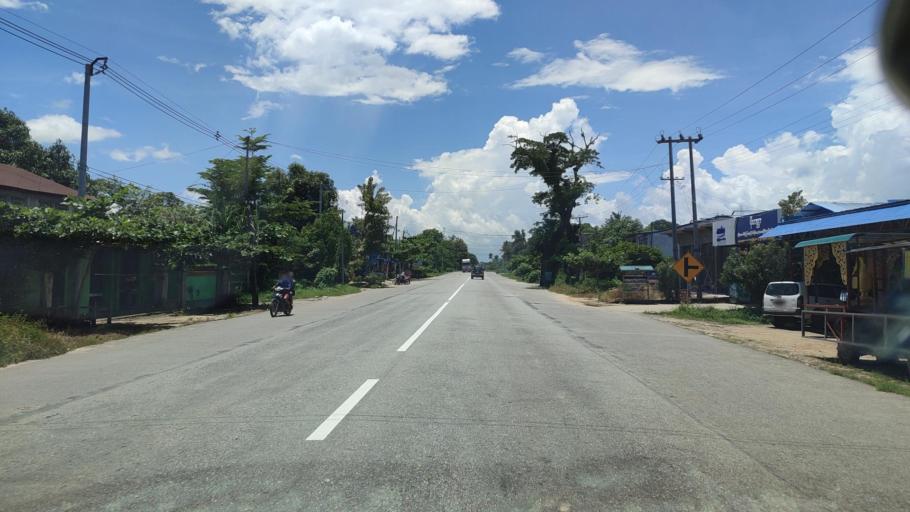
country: MM
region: Bago
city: Pyu
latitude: 18.7093
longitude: 96.4080
